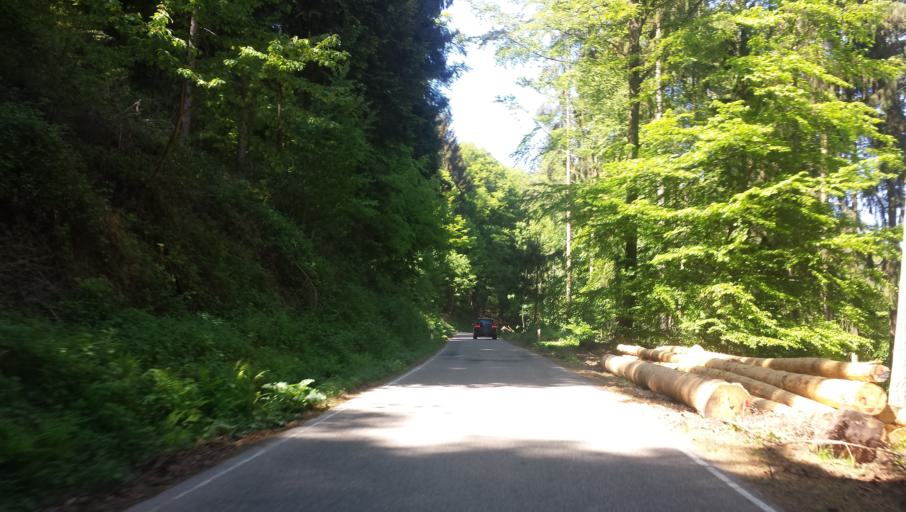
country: DE
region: Rheinland-Pfalz
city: Ramberg
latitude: 49.2751
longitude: 8.0275
